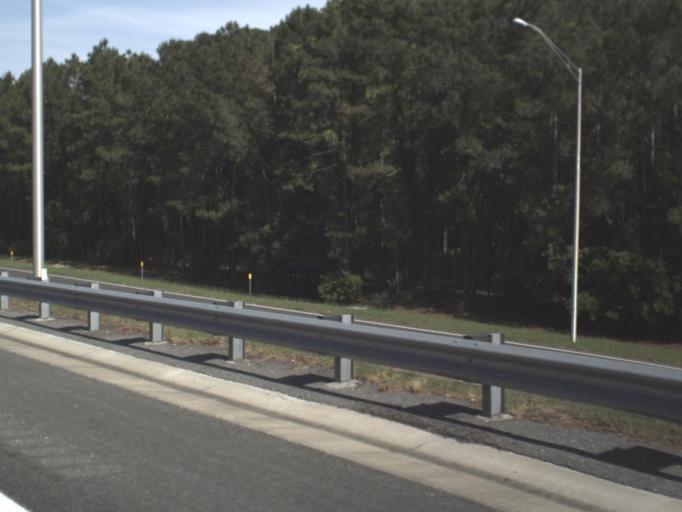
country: US
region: Florida
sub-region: Saint Johns County
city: Ponte Vedra Beach
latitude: 30.2515
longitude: -81.4644
